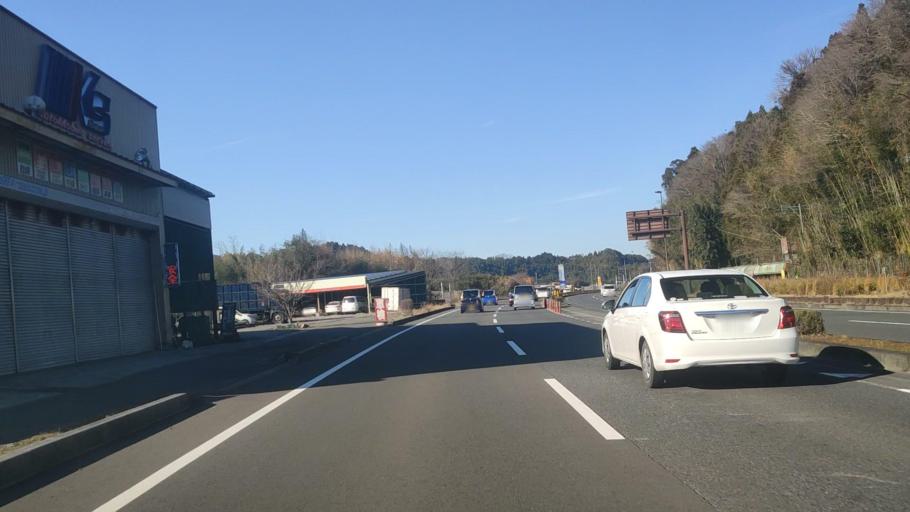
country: JP
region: Oita
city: Oita
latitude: 33.1148
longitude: 131.6546
